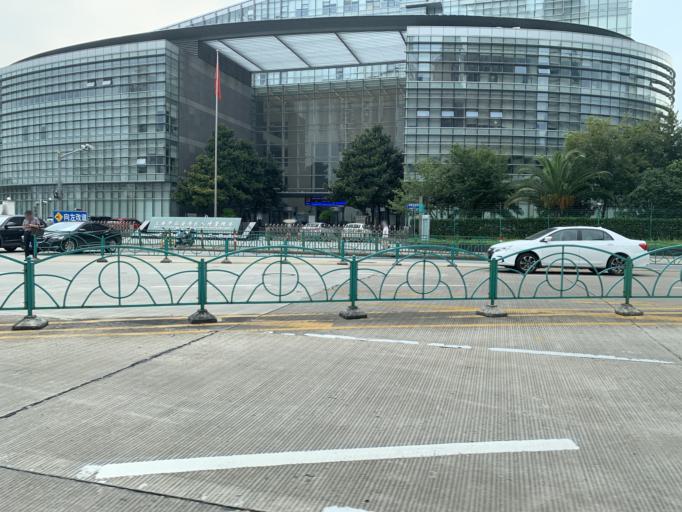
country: CN
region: Shanghai Shi
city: Huamu
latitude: 31.2245
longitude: 121.5463
